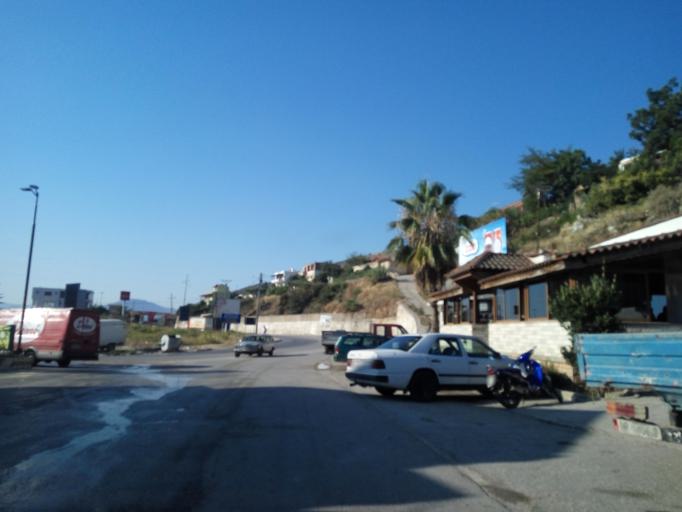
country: AL
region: Vlore
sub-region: Rrethi i Sarandes
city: Sarande
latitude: 39.8754
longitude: 20.0269
